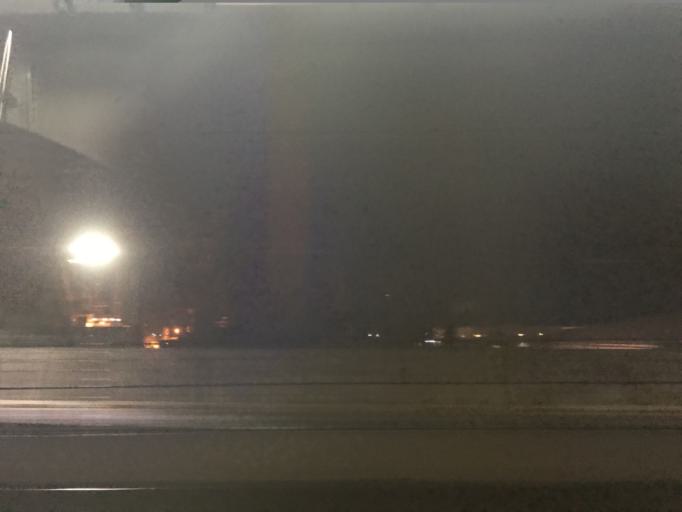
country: TR
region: Istanbul
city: Pendik
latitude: 40.8664
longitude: 29.2640
